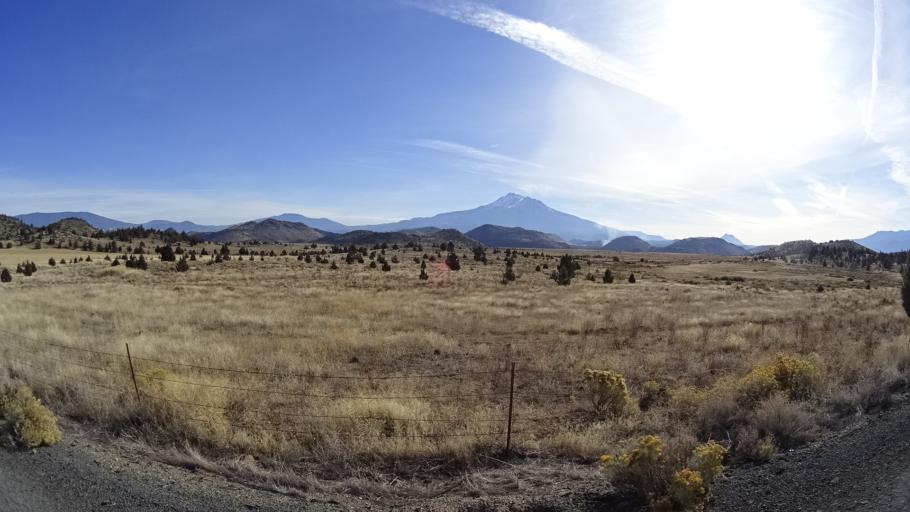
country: US
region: California
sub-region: Siskiyou County
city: Weed
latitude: 41.5578
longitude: -122.4716
